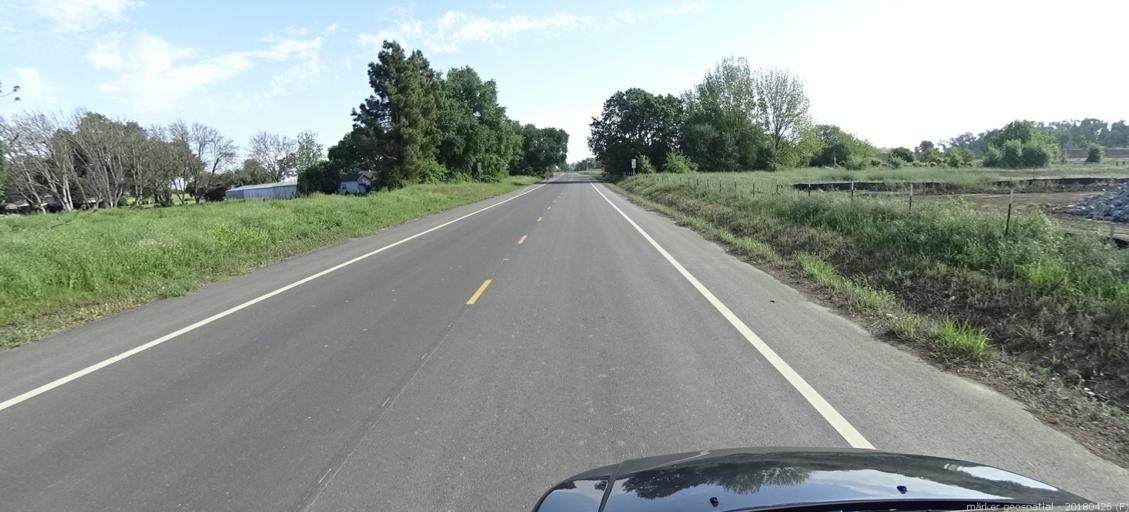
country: US
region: California
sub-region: Yolo County
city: West Sacramento
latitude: 38.5274
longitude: -121.5355
